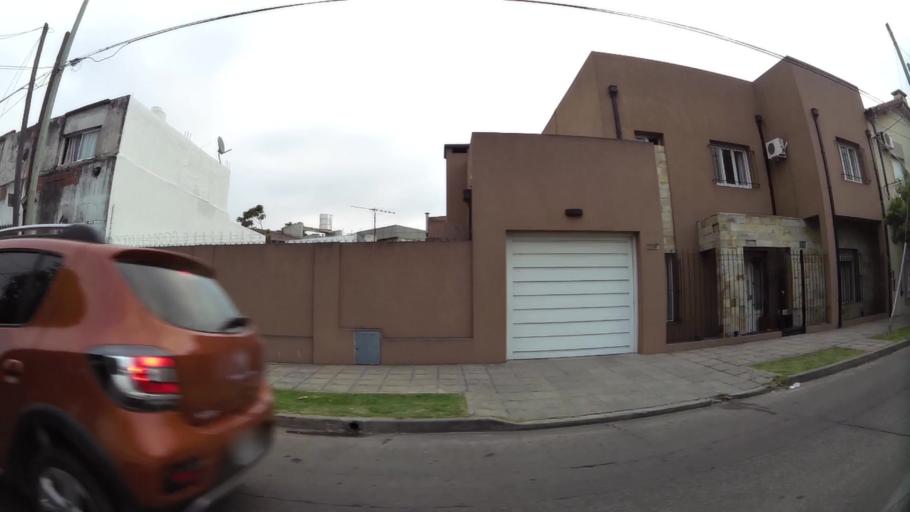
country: AR
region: Buenos Aires
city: San Justo
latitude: -34.6458
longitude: -58.5826
